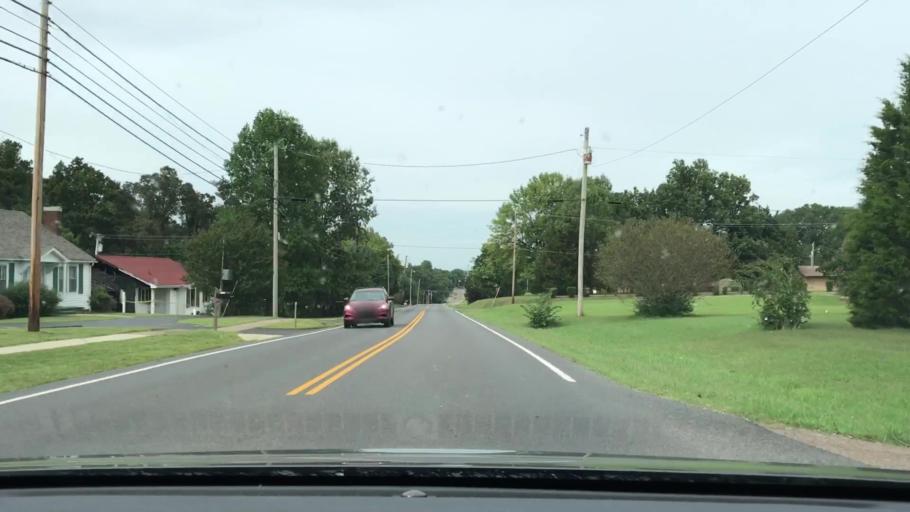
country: US
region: Kentucky
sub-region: Marshall County
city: Benton
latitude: 36.8469
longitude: -88.3499
